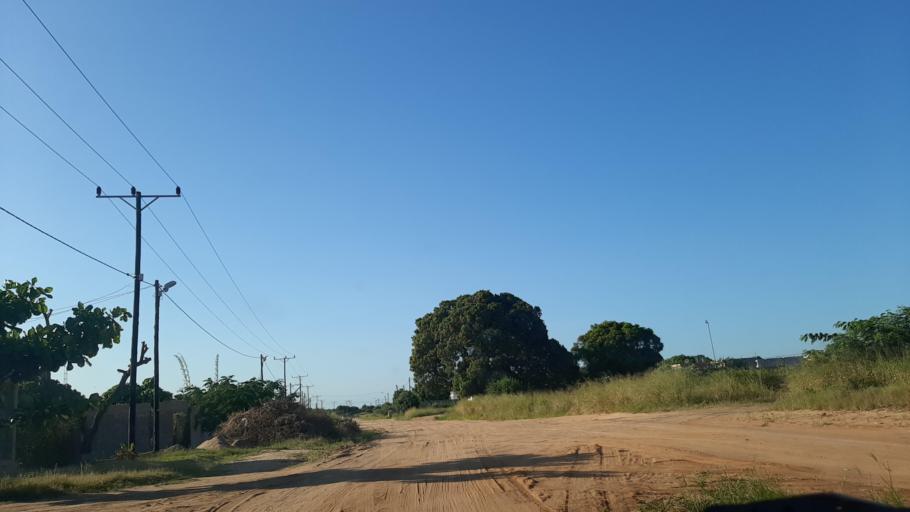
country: MZ
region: Maputo City
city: Maputo
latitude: -25.7689
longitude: 32.5481
